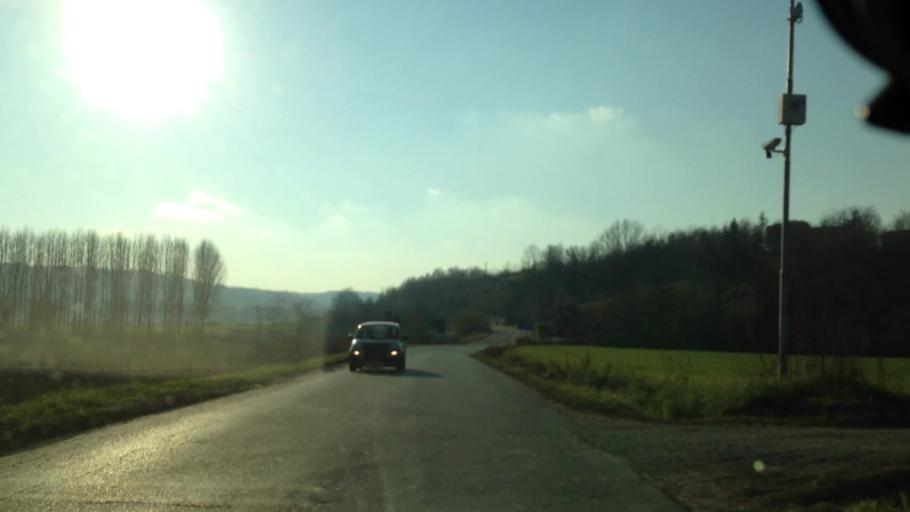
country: IT
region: Piedmont
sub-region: Provincia di Alessandria
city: Masio
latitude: 44.8455
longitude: 8.3955
